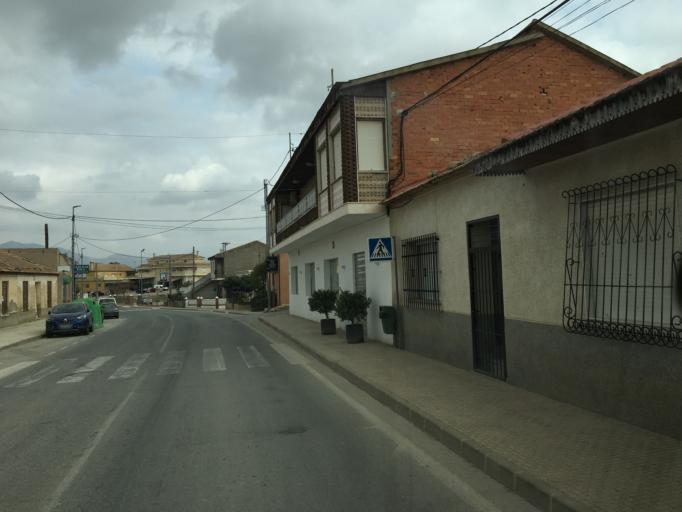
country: ES
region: Murcia
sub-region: Murcia
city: Beniel
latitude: 38.0242
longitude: -0.9808
